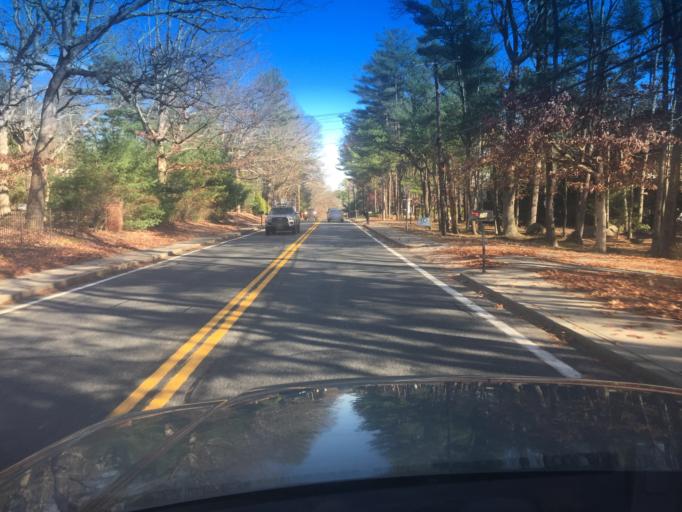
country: US
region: Rhode Island
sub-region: Providence County
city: Greenville
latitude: 41.8655
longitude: -71.5638
